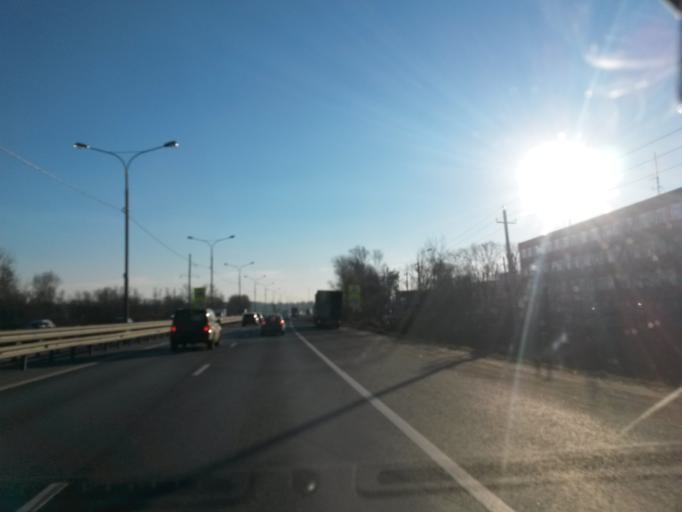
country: RU
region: Moskovskaya
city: Pushkino
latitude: 56.0018
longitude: 37.8777
